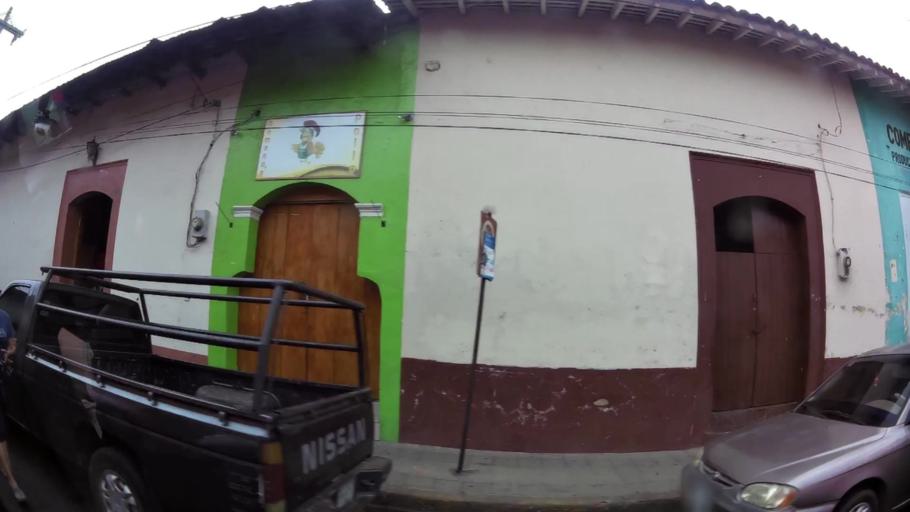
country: NI
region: Leon
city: Leon
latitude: 12.4349
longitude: -86.8760
